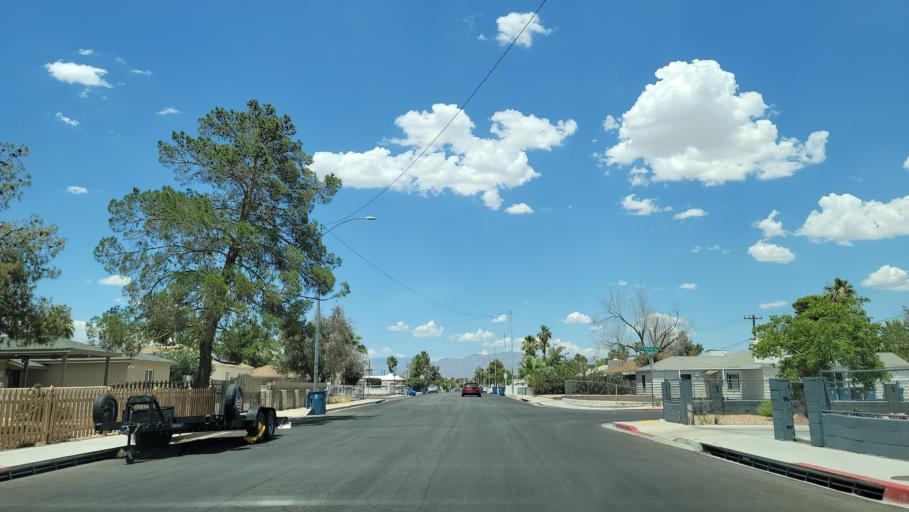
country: US
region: Nevada
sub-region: Clark County
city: Las Vegas
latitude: 36.1625
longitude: -115.1973
